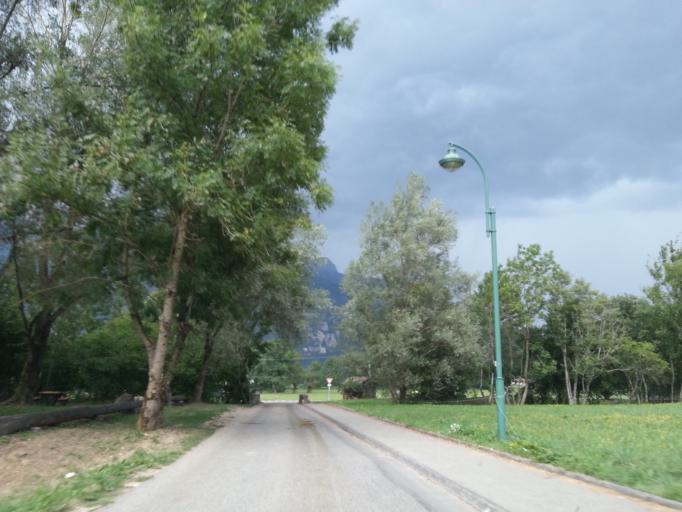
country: FR
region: Rhone-Alpes
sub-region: Departement de la Haute-Savoie
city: Doussard
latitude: 45.7857
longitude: 6.2087
